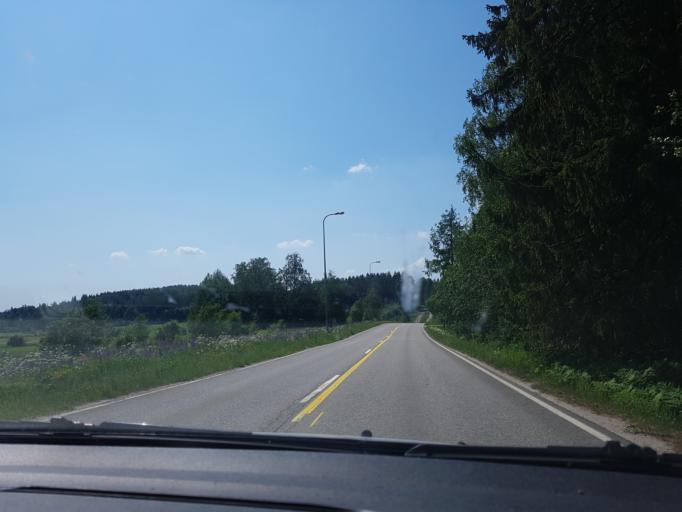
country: FI
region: Uusimaa
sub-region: Helsinki
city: Vihti
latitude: 60.3296
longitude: 24.4193
